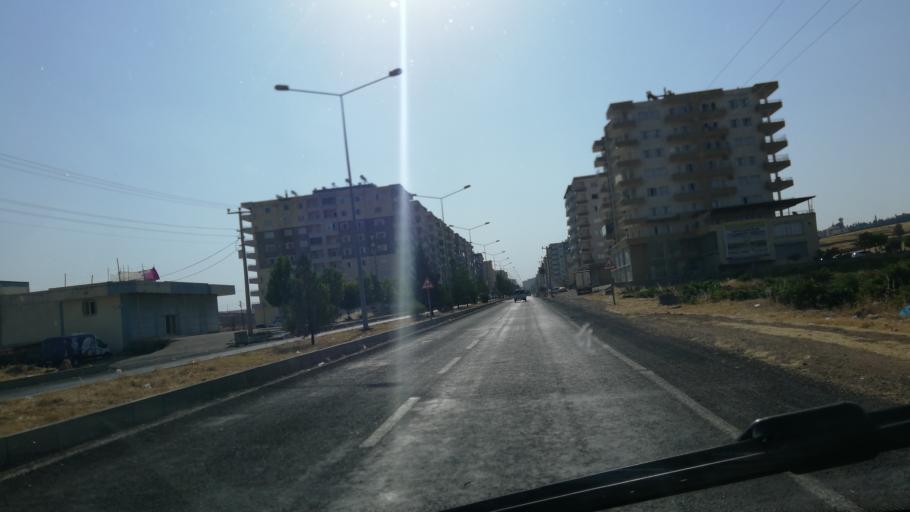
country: TR
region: Mardin
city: Midyat
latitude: 37.4351
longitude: 41.3238
